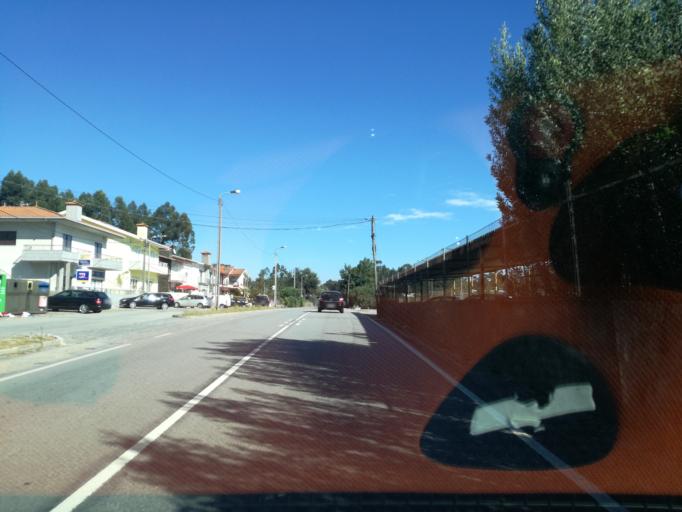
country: PT
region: Porto
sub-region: Trofa
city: Sao Romao do Coronado
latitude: 41.2855
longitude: -8.5928
